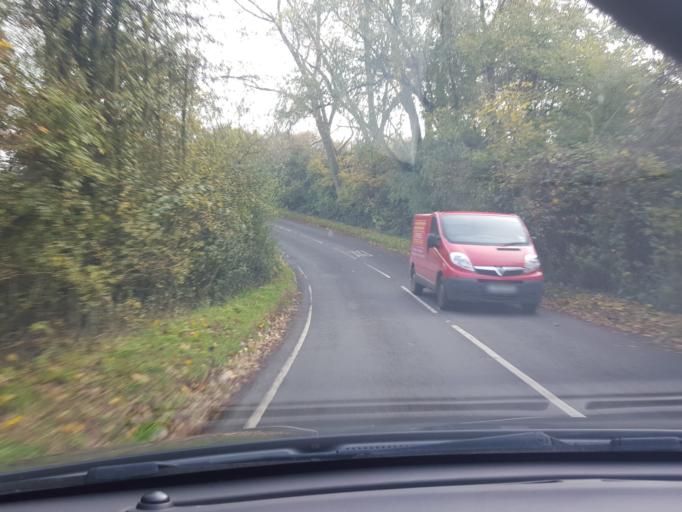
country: GB
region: England
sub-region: Essex
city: Mistley
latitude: 51.9345
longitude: 1.1231
